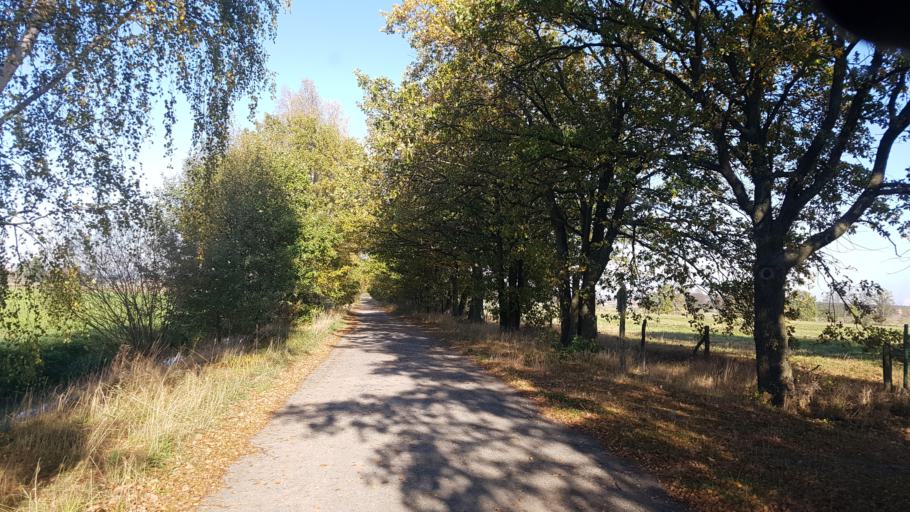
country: DE
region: Brandenburg
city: Ruckersdorf
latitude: 51.5556
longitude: 13.5405
